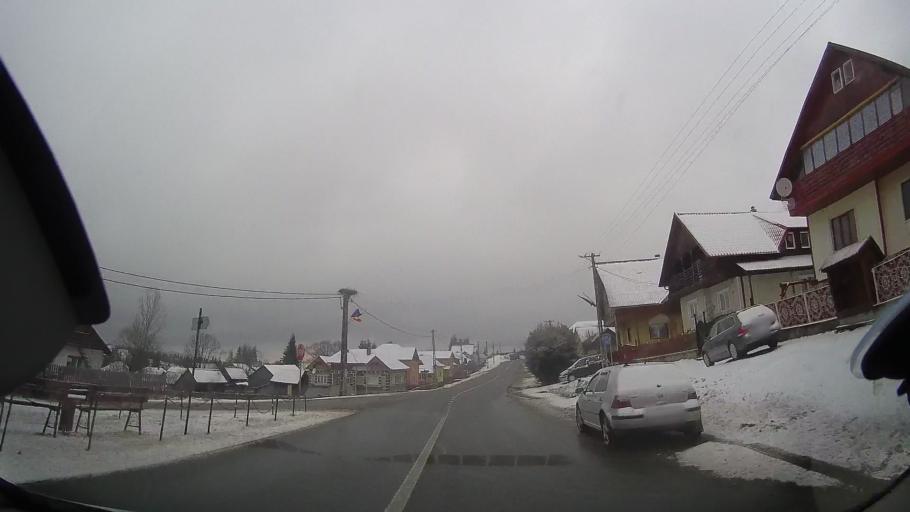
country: RO
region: Cluj
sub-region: Comuna Belis
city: Belis
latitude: 46.6838
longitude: 23.0333
